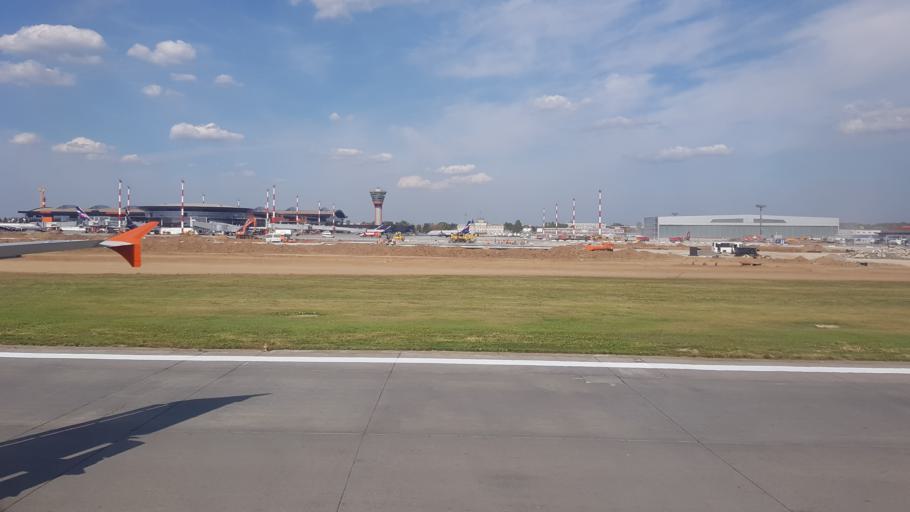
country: RU
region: Moskovskaya
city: Lobnya
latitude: 55.9752
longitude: 37.4223
